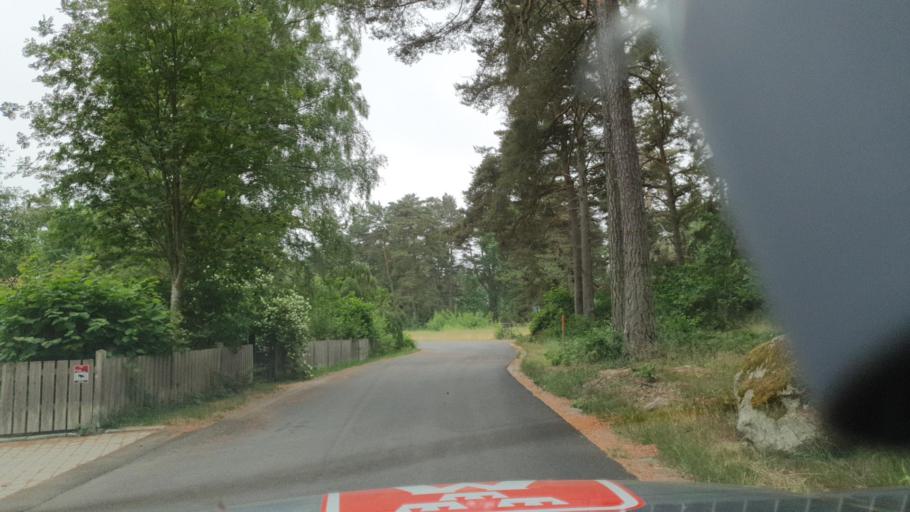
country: SE
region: Kalmar
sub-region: Kalmar Kommun
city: Rinkabyholm
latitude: 56.6494
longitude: 16.2682
